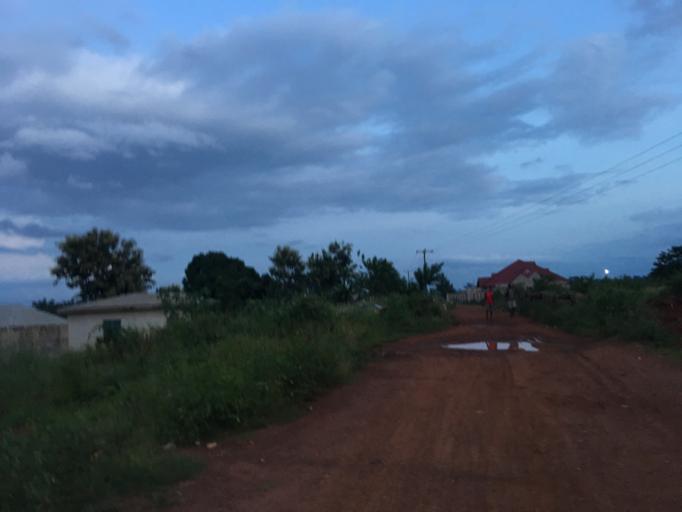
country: GH
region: Western
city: Bibiani
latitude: 6.7855
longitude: -2.5161
